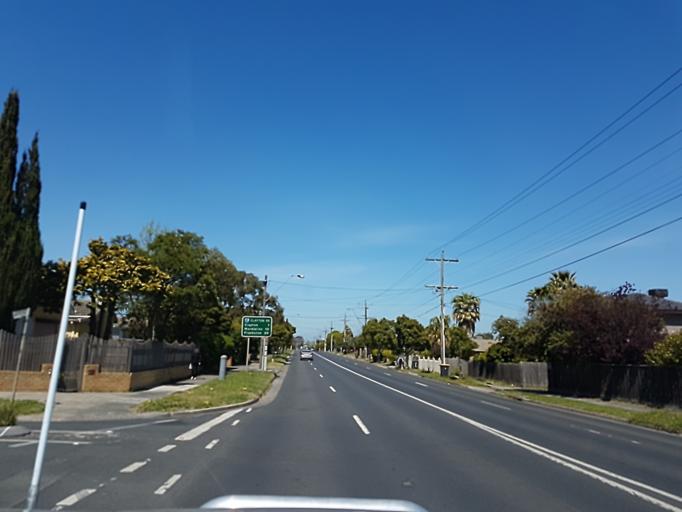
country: AU
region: Victoria
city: Clayton
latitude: -37.9150
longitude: 145.1217
